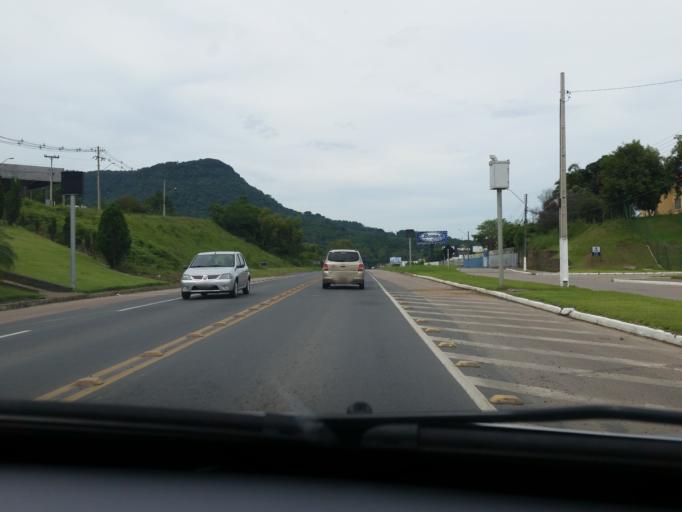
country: BR
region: Santa Catarina
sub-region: Rio Do Sul
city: Rio do Sul
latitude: -27.1962
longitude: -49.6267
